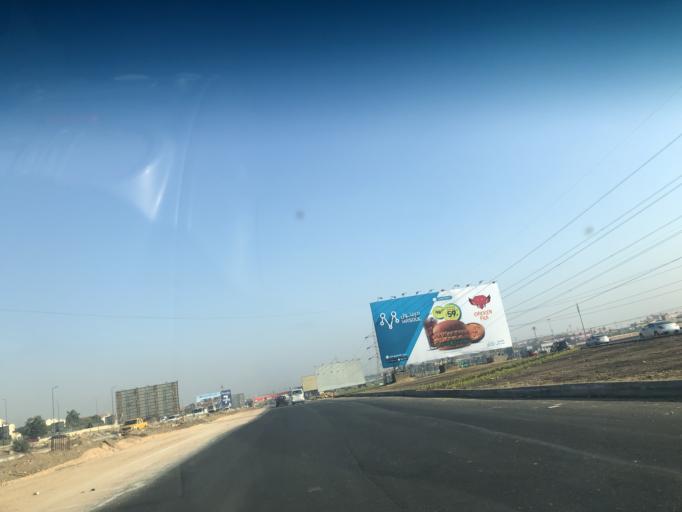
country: EG
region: Al Jizah
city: Madinat Sittah Uktubar
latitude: 29.9726
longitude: 31.0063
